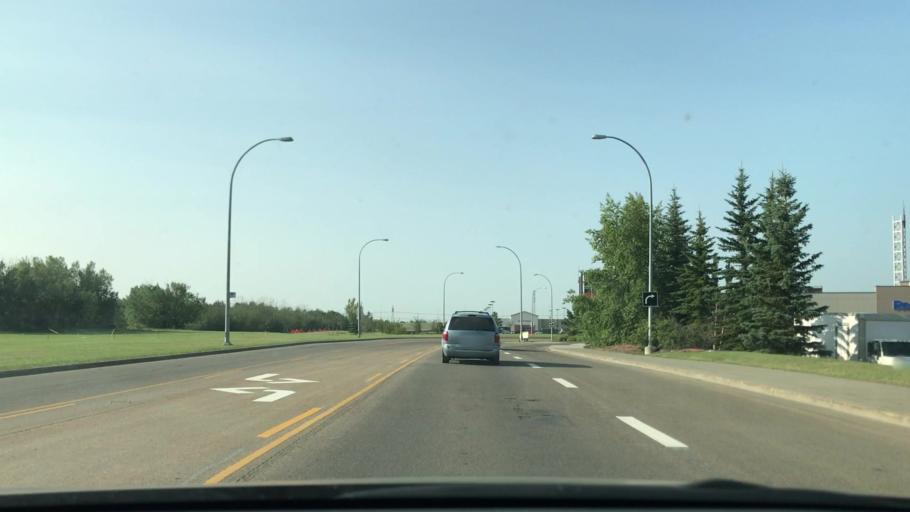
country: CA
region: Alberta
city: Edmonton
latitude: 53.4450
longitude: -113.4813
